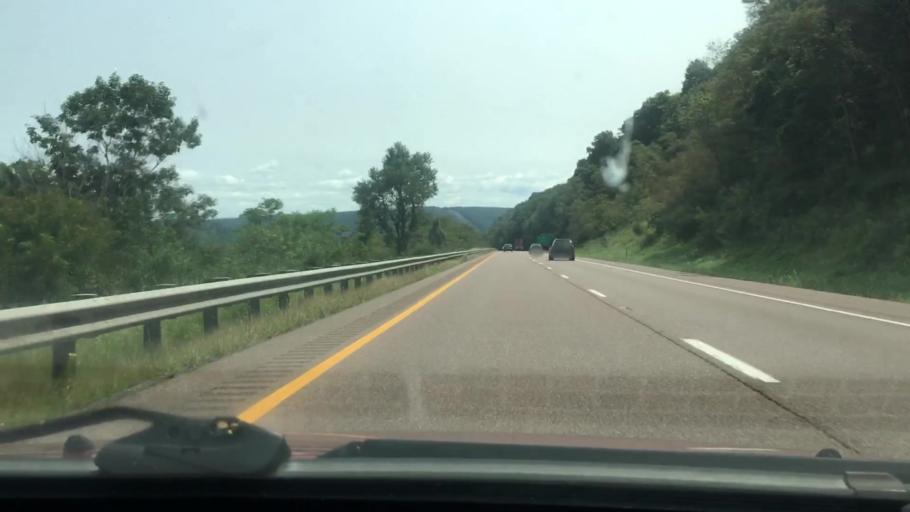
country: US
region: Maryland
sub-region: Allegany County
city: Cresaptown
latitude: 39.6405
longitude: -78.8681
